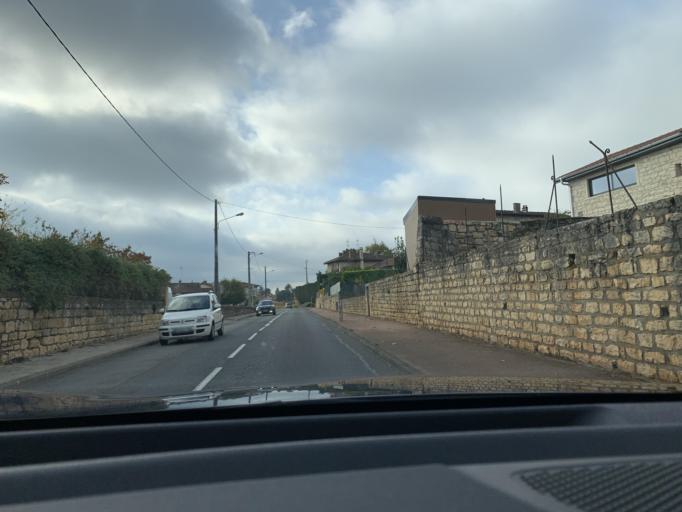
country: FR
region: Rhone-Alpes
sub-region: Departement du Rhone
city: Lucenay
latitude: 45.9107
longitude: 4.7017
